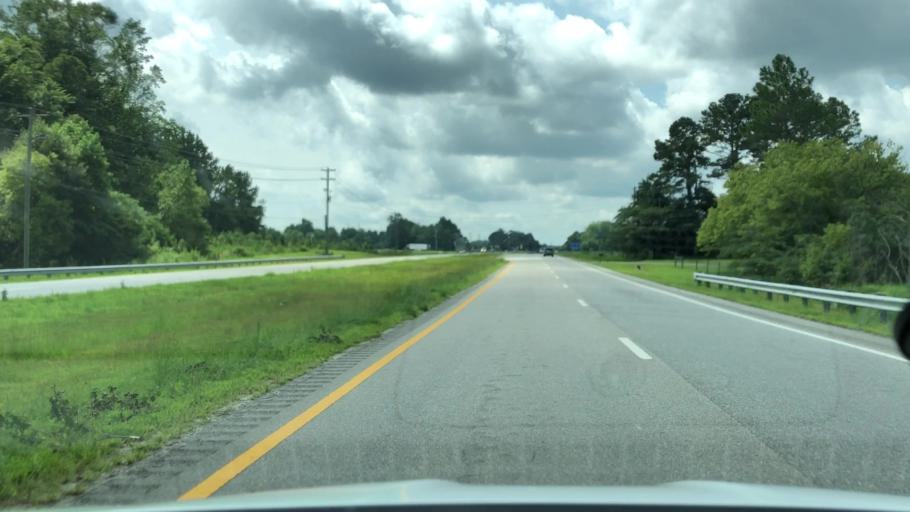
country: US
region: North Carolina
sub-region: Beaufort County
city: Washington
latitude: 35.4951
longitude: -77.1056
